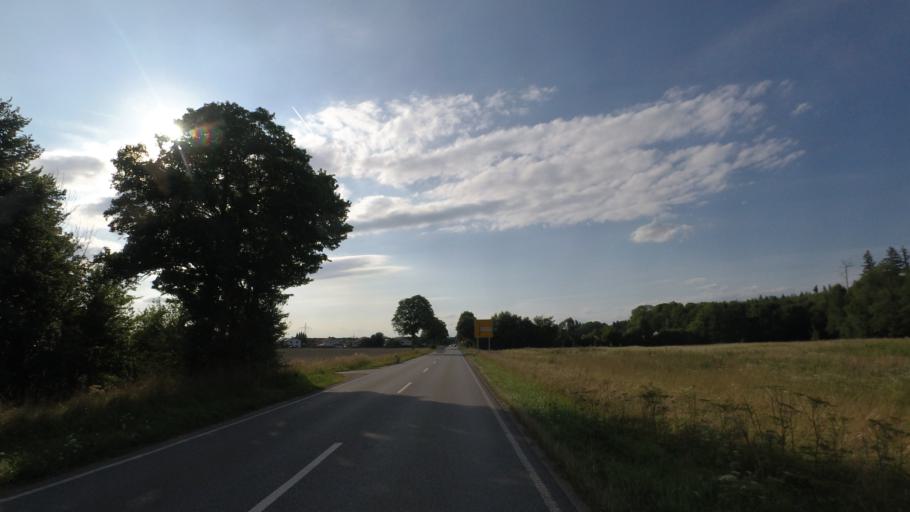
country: DE
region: Bavaria
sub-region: Upper Bavaria
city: Chieming
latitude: 47.9043
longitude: 12.5433
